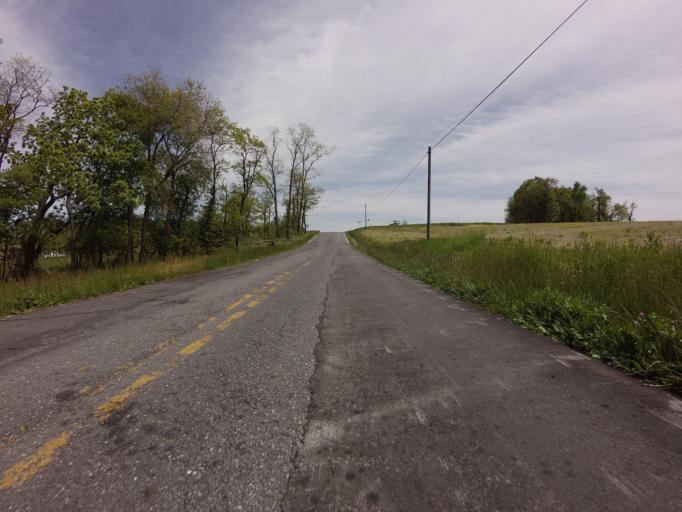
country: US
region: Maryland
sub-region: Frederick County
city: Linganore
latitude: 39.5126
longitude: -77.2126
